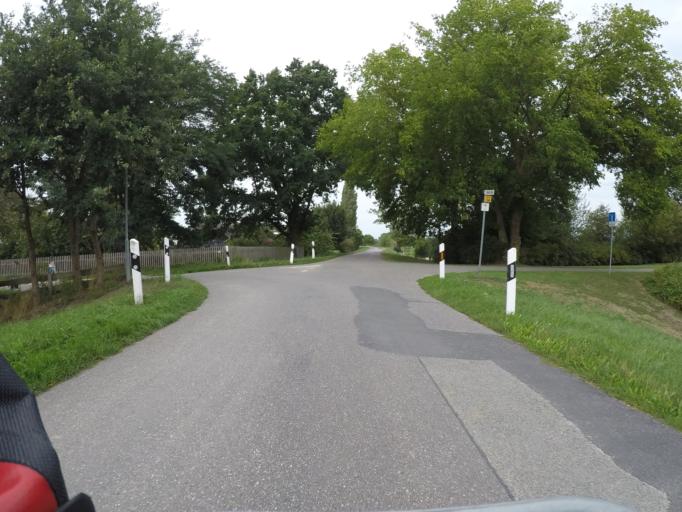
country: DE
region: Lower Saxony
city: Winsen
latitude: 53.3885
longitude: 10.1993
